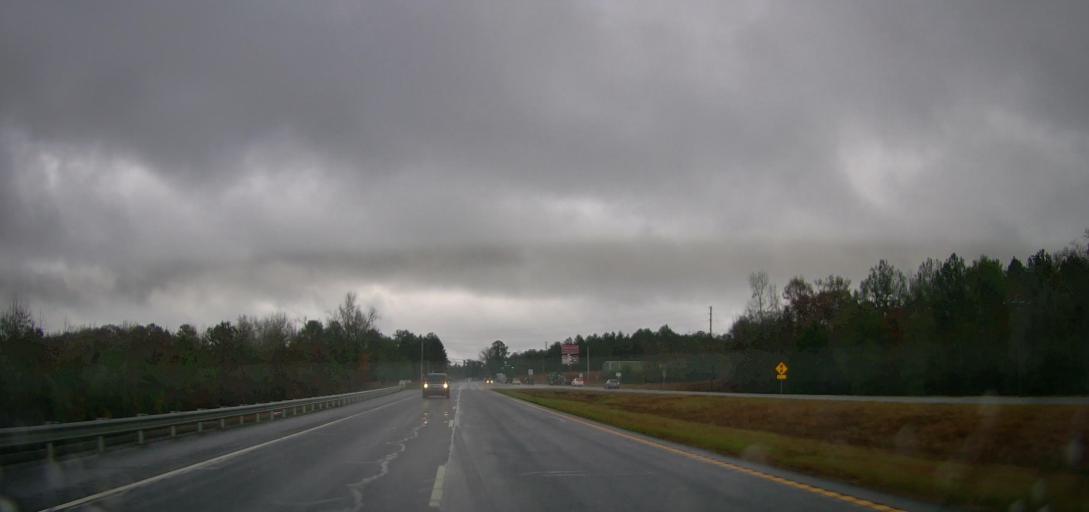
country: US
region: Georgia
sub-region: Clarke County
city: Country Club Estates
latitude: 34.0252
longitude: -83.3989
